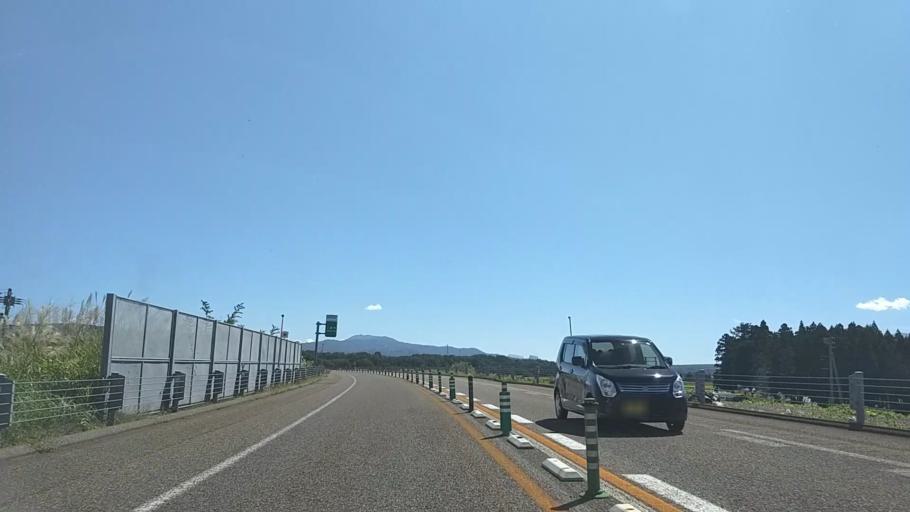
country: JP
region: Niigata
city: Arai
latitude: 36.9939
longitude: 138.2073
